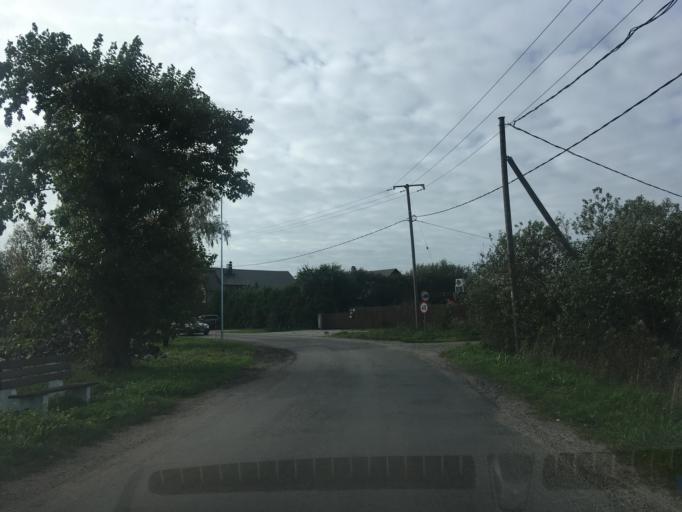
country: EE
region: Harju
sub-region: Joelaehtme vald
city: Loo
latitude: 59.4458
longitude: 24.9725
